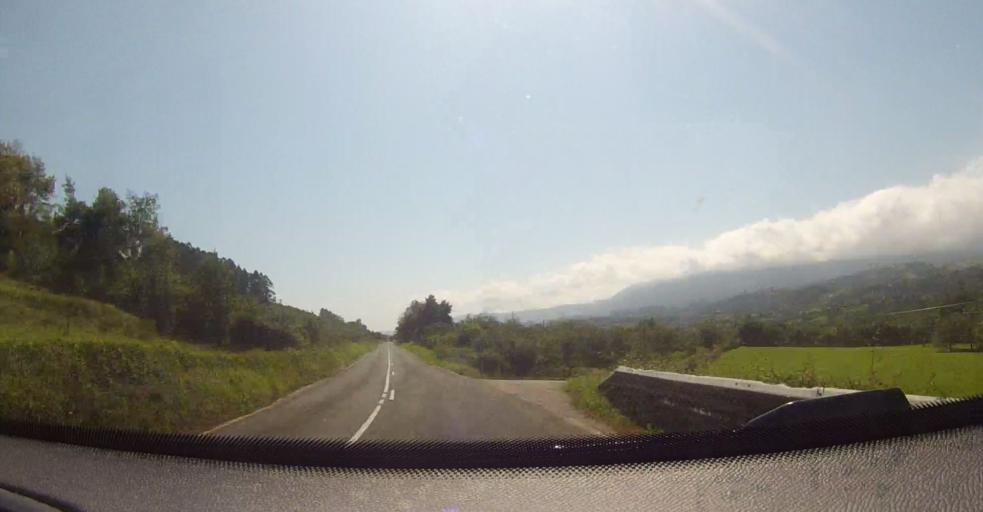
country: ES
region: Asturias
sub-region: Province of Asturias
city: Colunga
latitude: 43.4897
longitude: -5.3108
